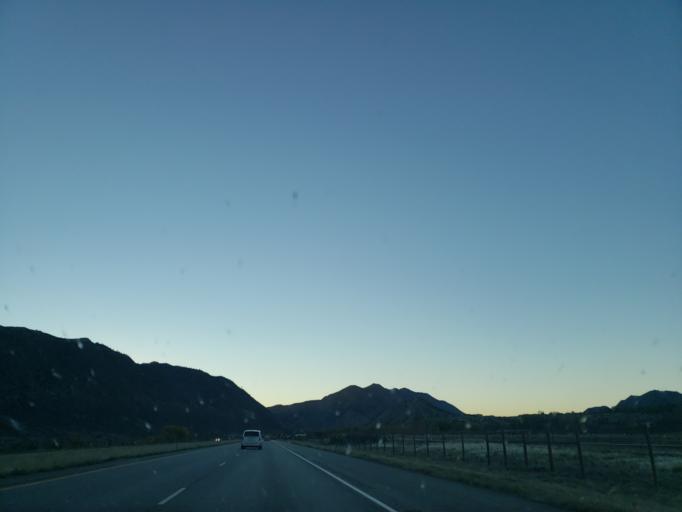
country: US
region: Colorado
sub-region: Garfield County
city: New Castle
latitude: 39.5660
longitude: -107.4994
